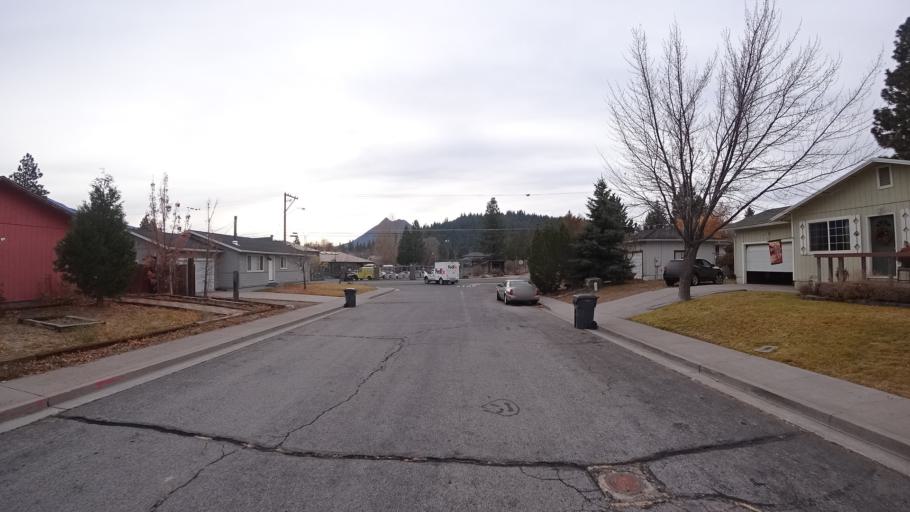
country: US
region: California
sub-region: Siskiyou County
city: Weed
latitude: 41.4169
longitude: -122.3877
